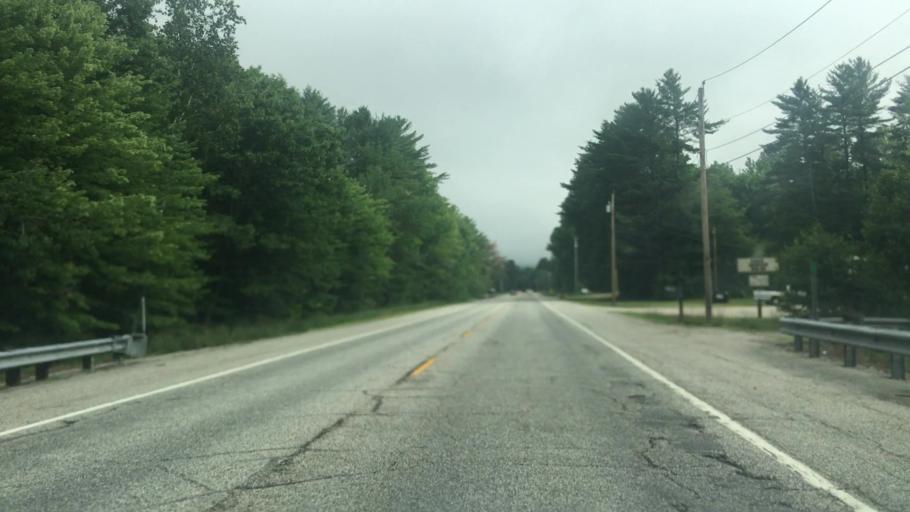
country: US
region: Maine
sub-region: Oxford County
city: Paris
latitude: 44.2684
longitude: -70.5147
